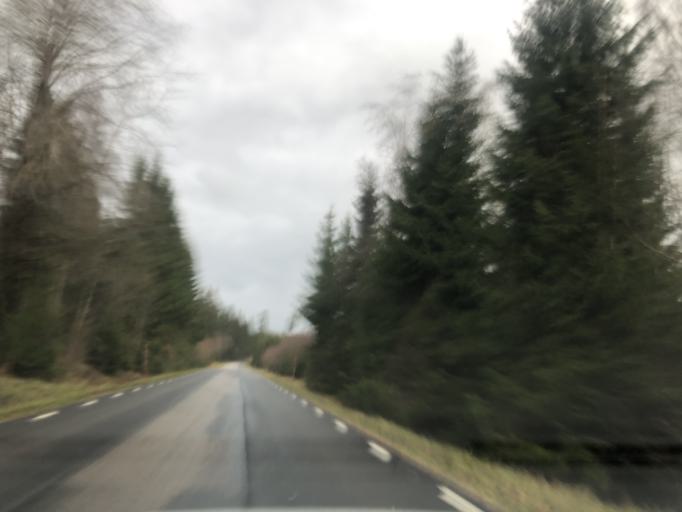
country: SE
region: Vaestra Goetaland
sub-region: Boras Kommun
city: Dalsjofors
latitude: 57.8142
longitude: 13.1986
